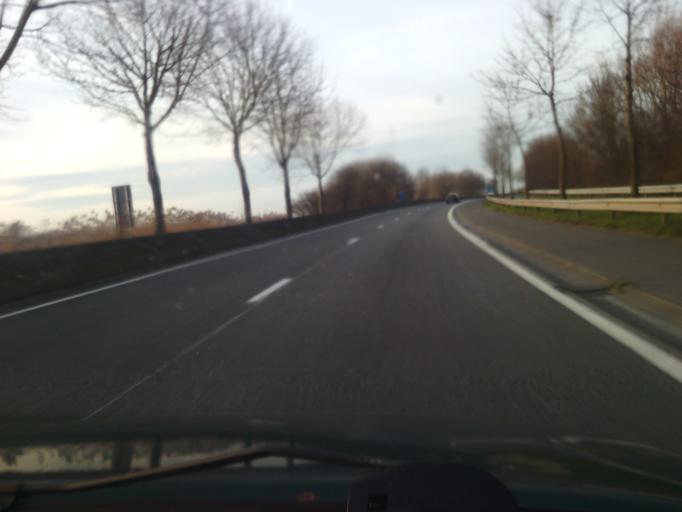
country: BE
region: Flanders
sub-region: Provincie Oost-Vlaanderen
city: Gent
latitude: 51.0345
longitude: 3.6871
